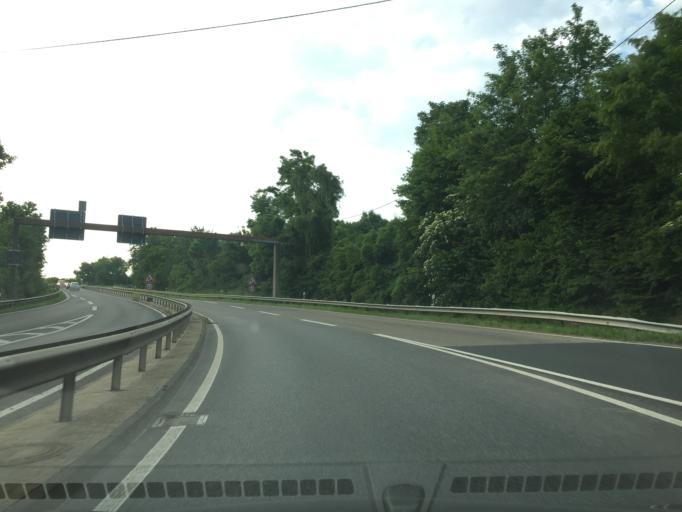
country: DE
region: Rheinland-Pfalz
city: Bendorf
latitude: 50.4126
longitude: 7.5850
